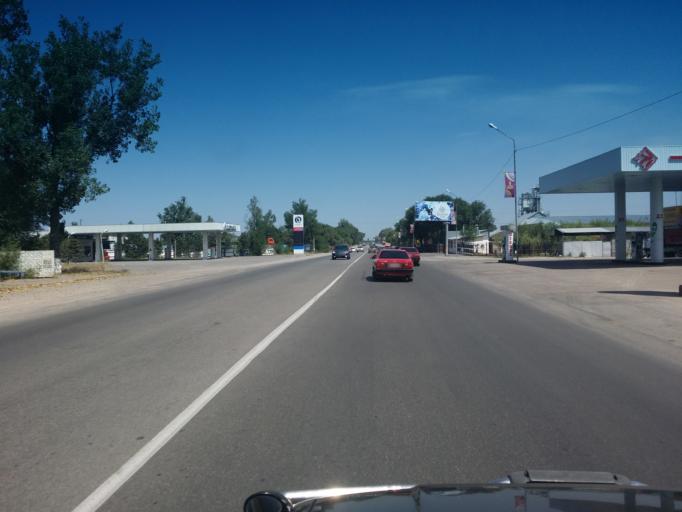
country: KZ
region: Almaty Oblysy
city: Talghar
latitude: 43.4061
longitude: 77.2333
